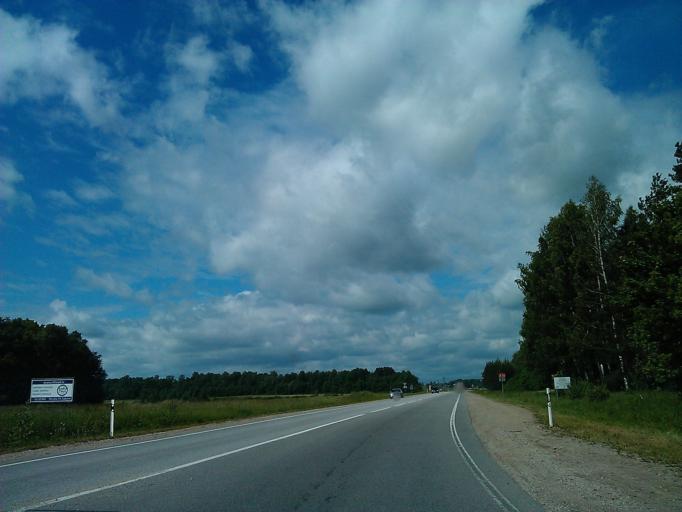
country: LV
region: Tukuma Rajons
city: Tukums
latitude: 56.9495
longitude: 23.1123
